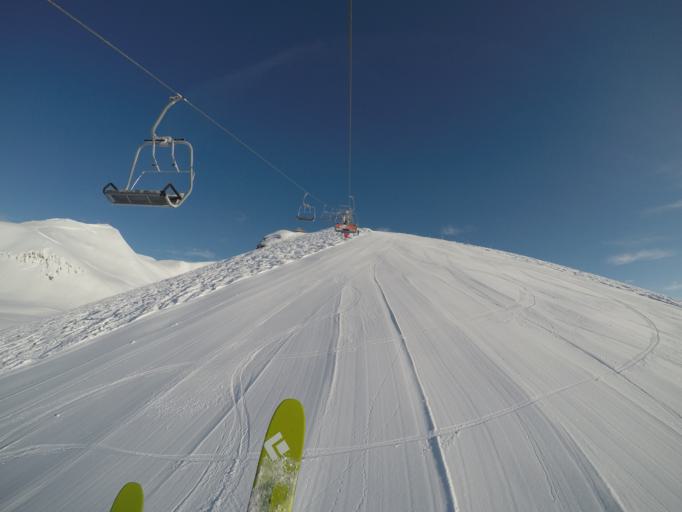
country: GE
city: Gudauri
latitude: 42.4952
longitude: 44.5058
